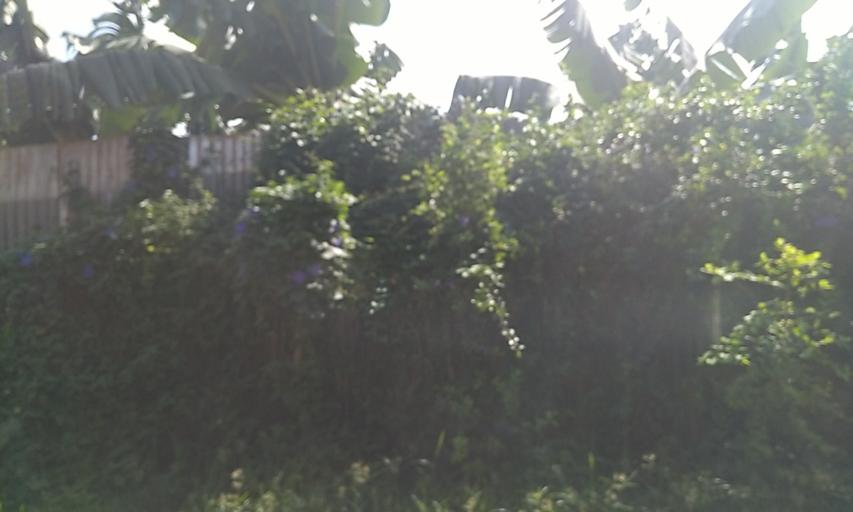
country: UG
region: Central Region
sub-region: Wakiso District
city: Kireka
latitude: 0.3546
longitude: 32.6193
